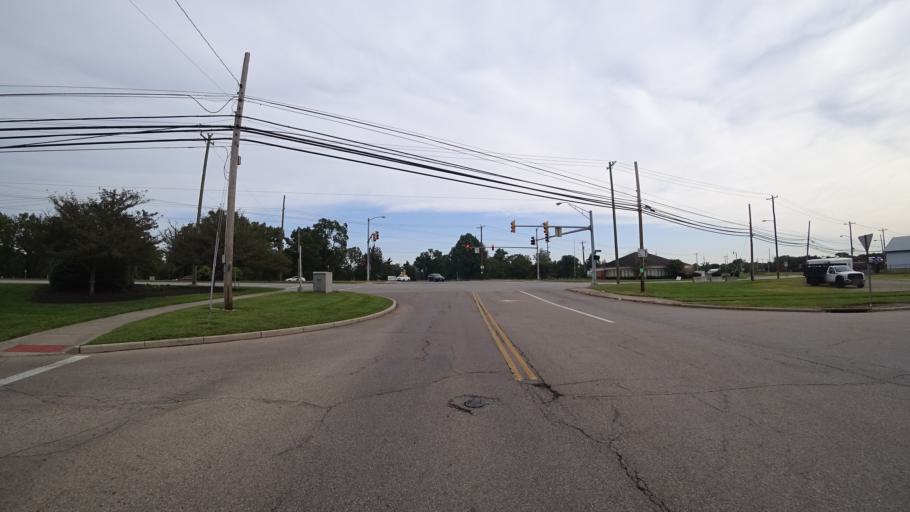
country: US
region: Ohio
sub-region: Butler County
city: Hamilton
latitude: 39.4014
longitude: -84.5407
